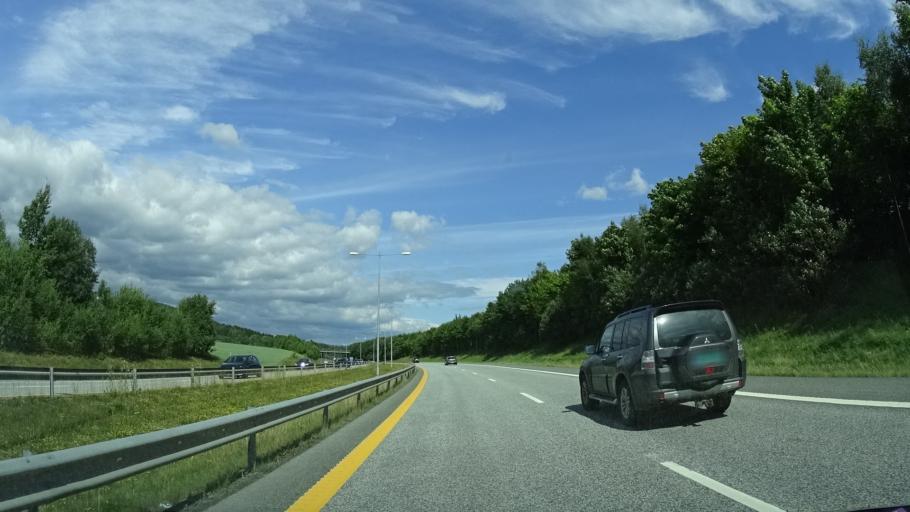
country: NO
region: Buskerud
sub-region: Drammen
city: Skoger
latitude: 59.6801
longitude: 10.2463
